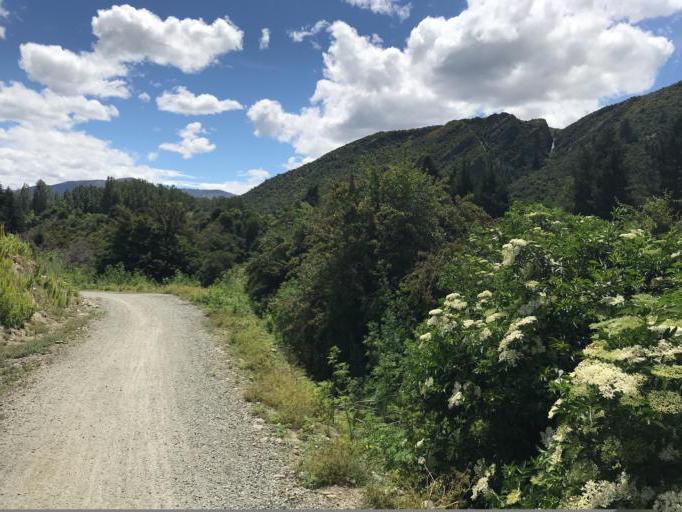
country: NZ
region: Otago
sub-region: Queenstown-Lakes District
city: Arrowtown
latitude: -44.9935
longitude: 168.8617
